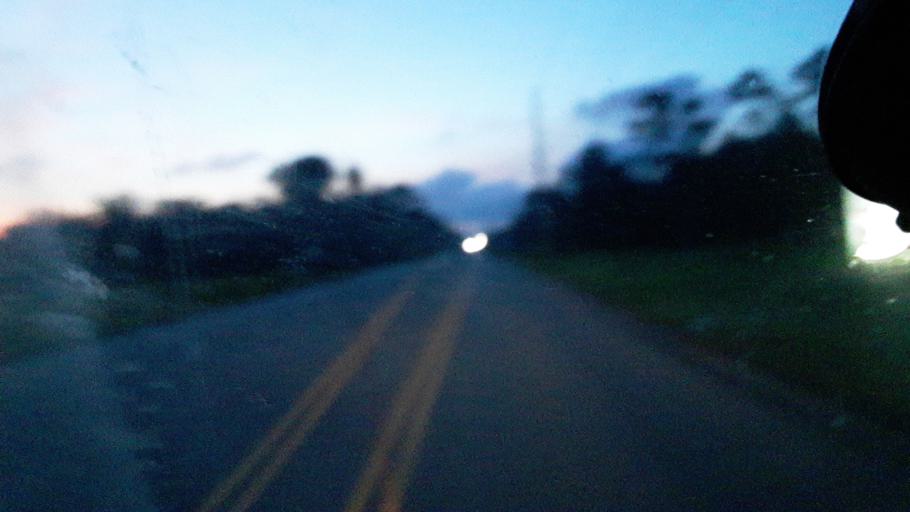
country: US
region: North Carolina
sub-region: Brunswick County
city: Oak Island
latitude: 33.9967
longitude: -78.2343
